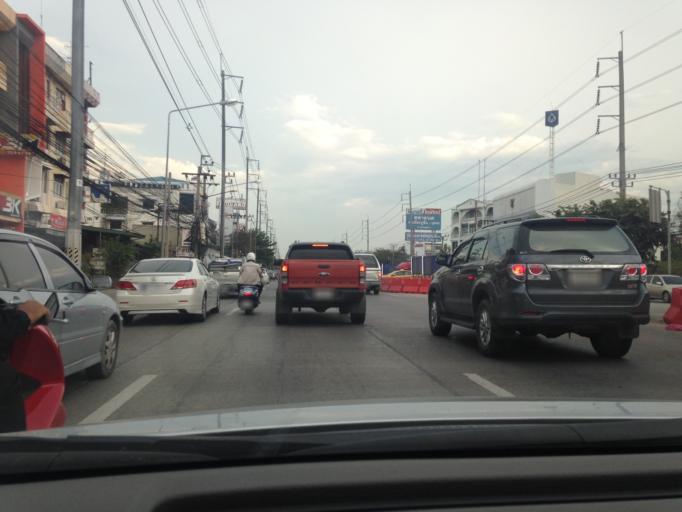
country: TH
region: Bangkok
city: Bang Khen
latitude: 13.8602
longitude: 100.6229
